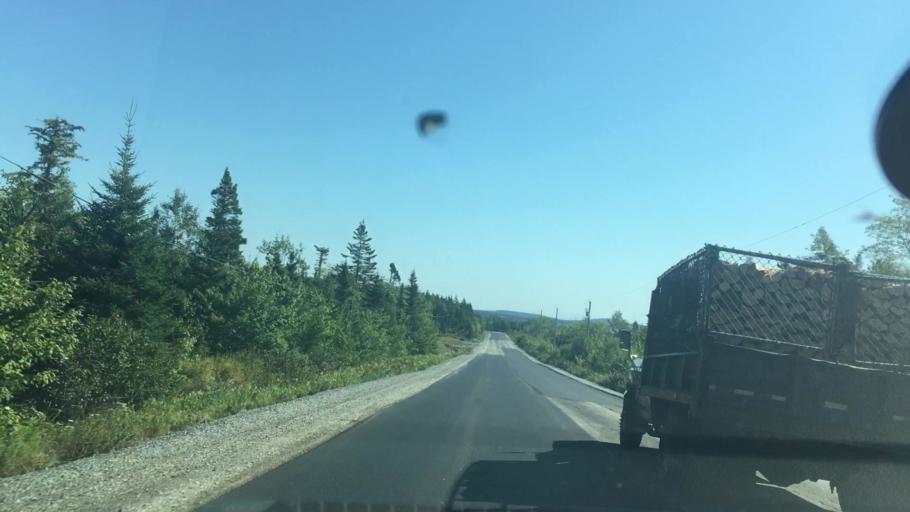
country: CA
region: Nova Scotia
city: New Glasgow
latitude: 44.8982
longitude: -62.4282
